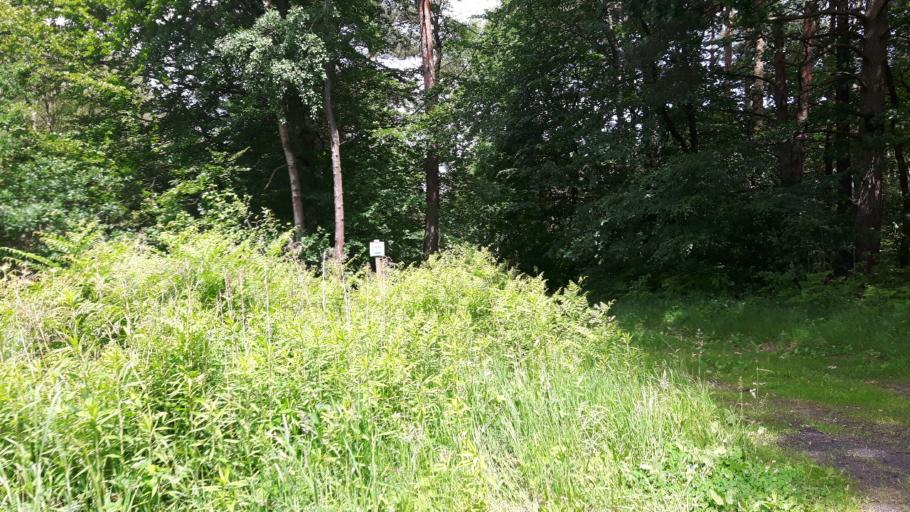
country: PL
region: West Pomeranian Voivodeship
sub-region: Powiat goleniowski
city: Goleniow
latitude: 53.6111
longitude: 14.8774
